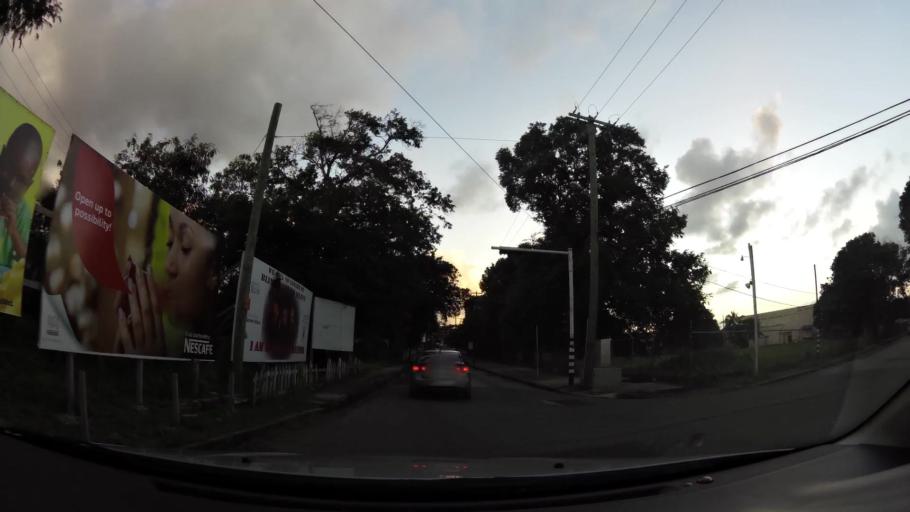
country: AG
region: Saint John
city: Saint John's
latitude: 17.1255
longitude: -61.8396
